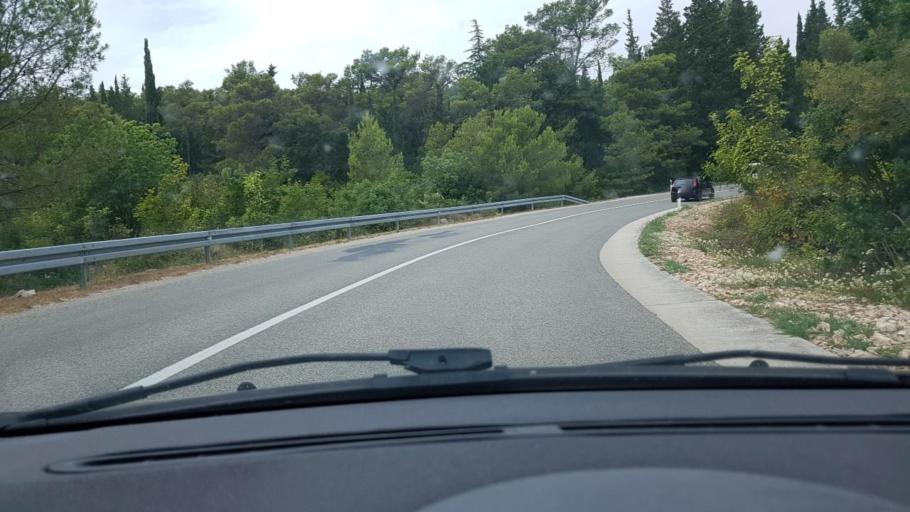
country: HR
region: Dubrovacko-Neretvanska
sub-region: Grad Korcula
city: Zrnovo
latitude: 42.9471
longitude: 17.0414
